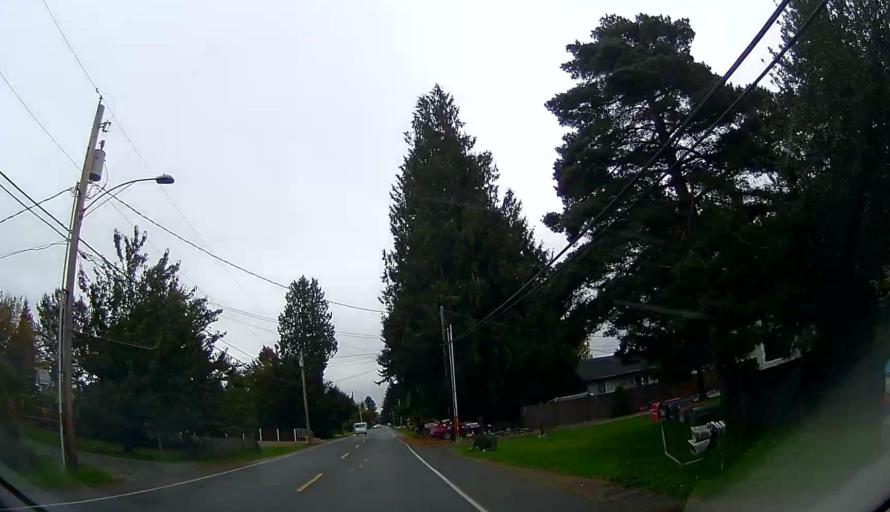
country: US
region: Washington
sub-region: Skagit County
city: Sedro-Woolley
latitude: 48.5032
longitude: -122.2176
